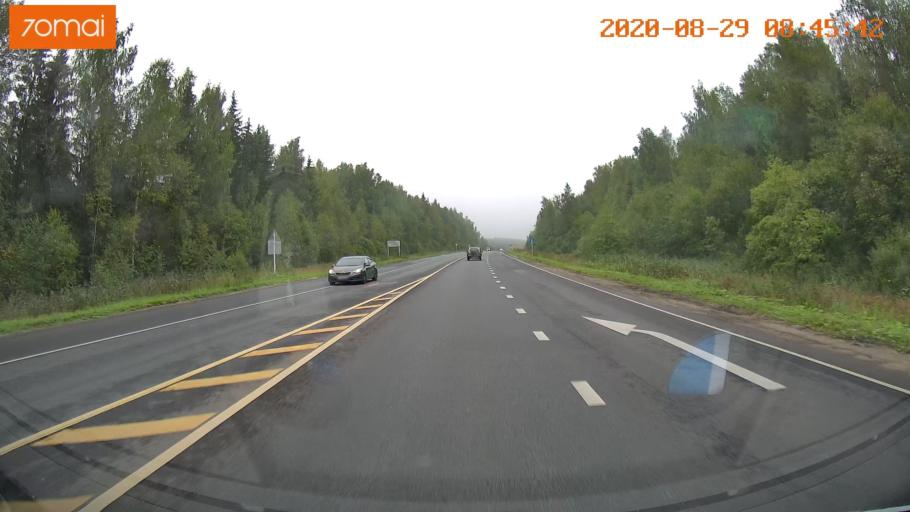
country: RU
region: Ivanovo
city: Rodniki
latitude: 57.1338
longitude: 41.8037
